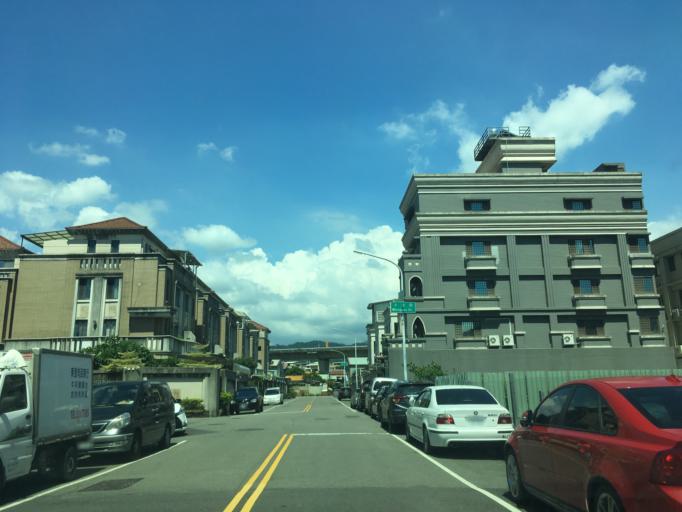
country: TW
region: Taiwan
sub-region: Taichung City
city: Taichung
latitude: 24.1461
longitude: 120.7102
